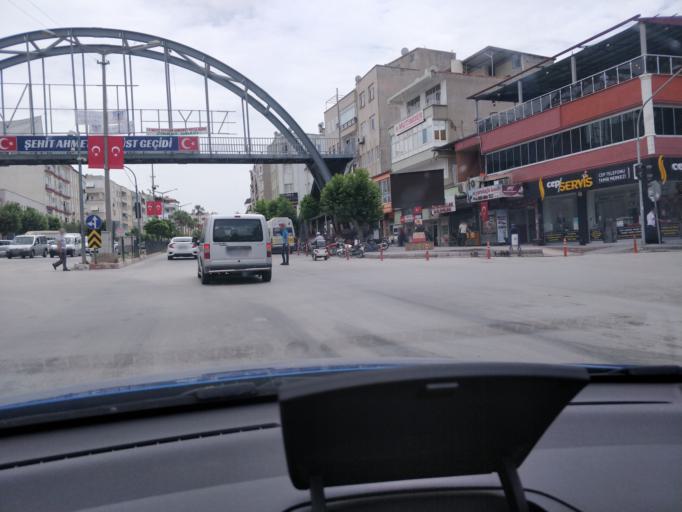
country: TR
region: Mersin
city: Mut
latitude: 36.6455
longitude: 33.4369
